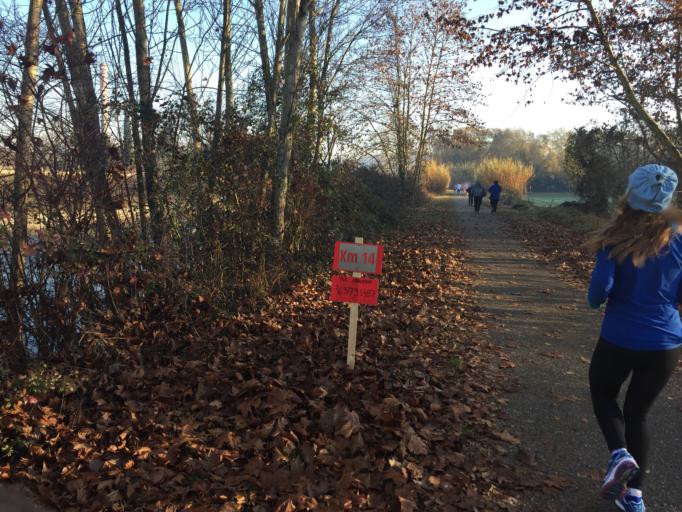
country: IT
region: Lombardy
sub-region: Provincia di Mantova
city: Monzambano
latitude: 45.3928
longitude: 10.7083
